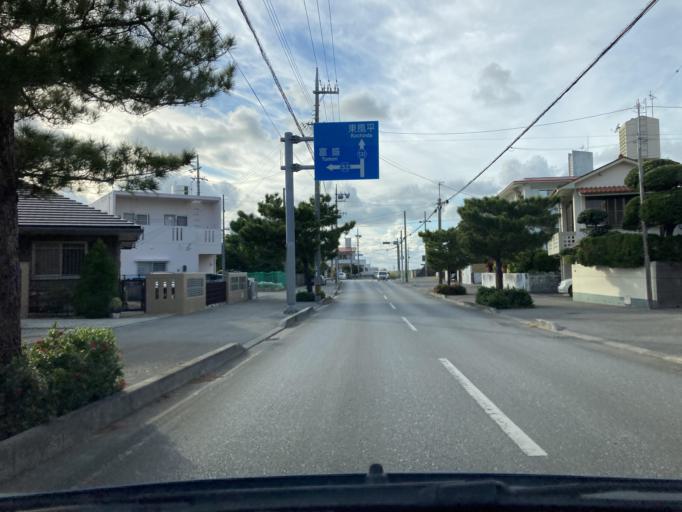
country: JP
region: Okinawa
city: Itoman
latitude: 26.1383
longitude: 127.7392
